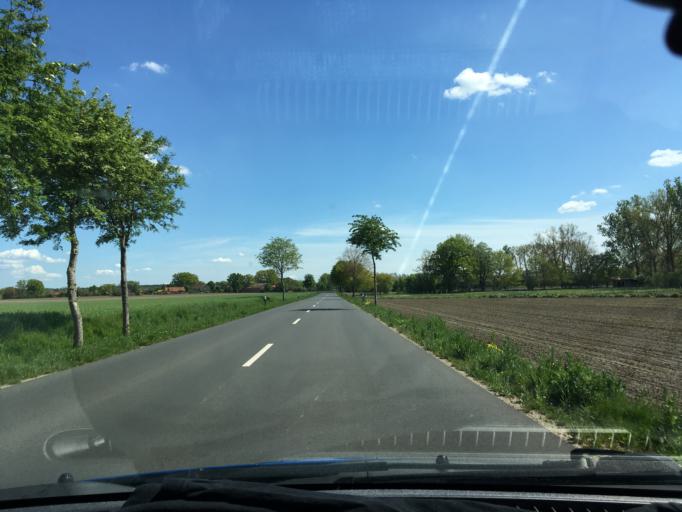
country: DE
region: Lower Saxony
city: Stoetze
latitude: 53.0764
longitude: 10.7637
